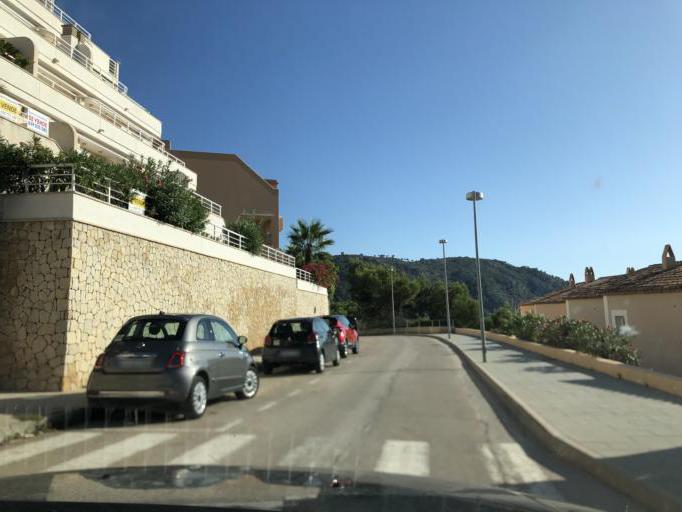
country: ES
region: Balearic Islands
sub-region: Illes Balears
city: Camp de Mar
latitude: 39.5394
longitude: 2.4184
